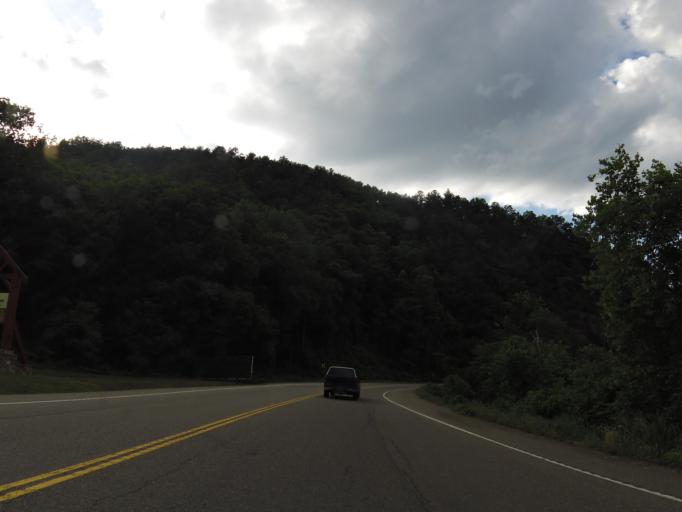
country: US
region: Tennessee
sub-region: Blount County
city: Wildwood
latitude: 35.6868
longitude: -83.7975
